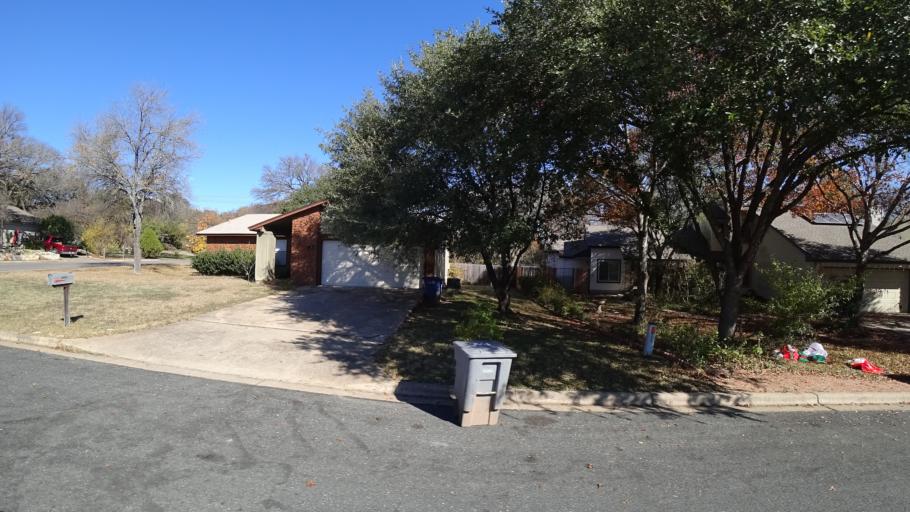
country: US
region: Texas
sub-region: Travis County
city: Wells Branch
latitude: 30.4186
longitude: -97.7113
